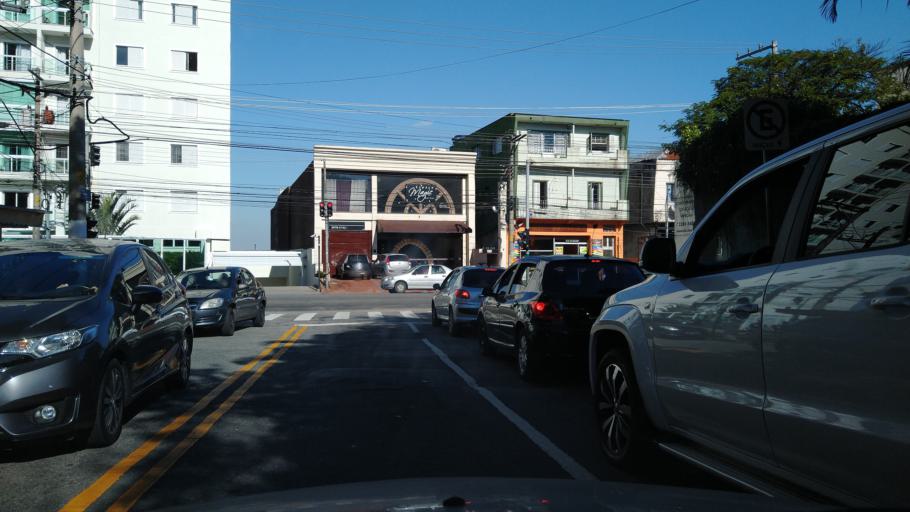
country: BR
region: Sao Paulo
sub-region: Sao Paulo
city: Sao Paulo
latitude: -23.4835
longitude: -46.6144
